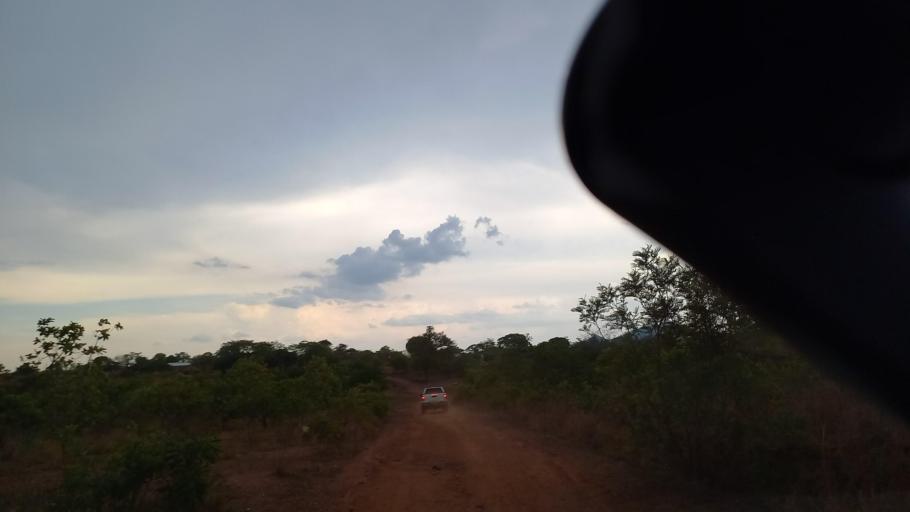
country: ZM
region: Lusaka
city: Kafue
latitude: -15.9858
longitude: 28.2650
